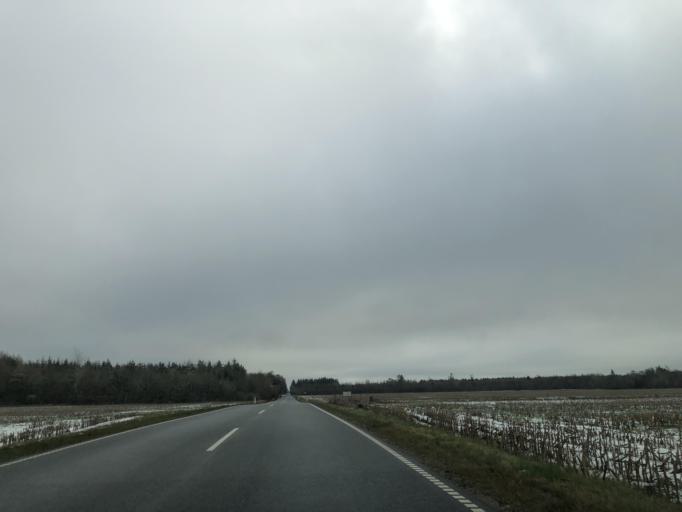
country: DK
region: Central Jutland
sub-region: Ikast-Brande Kommune
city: Brande
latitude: 55.9880
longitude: 9.2259
